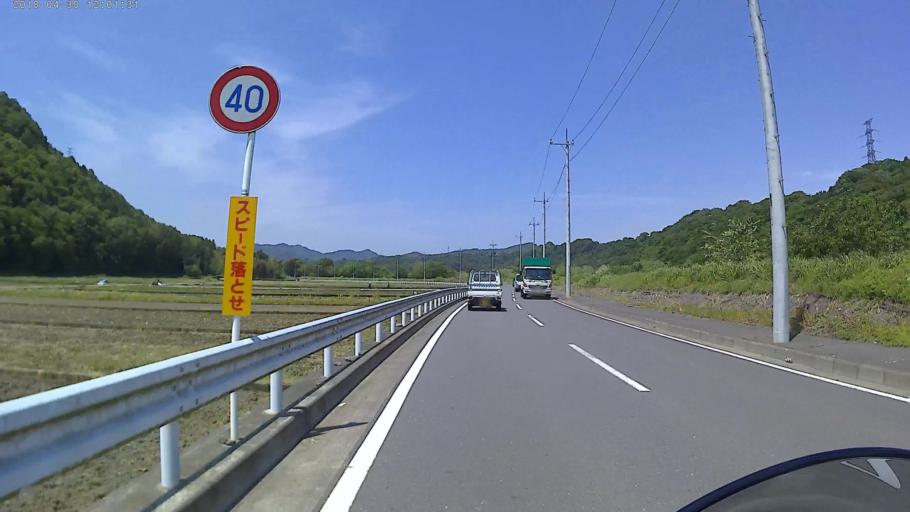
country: JP
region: Kanagawa
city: Zama
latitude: 35.5179
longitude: 139.3250
